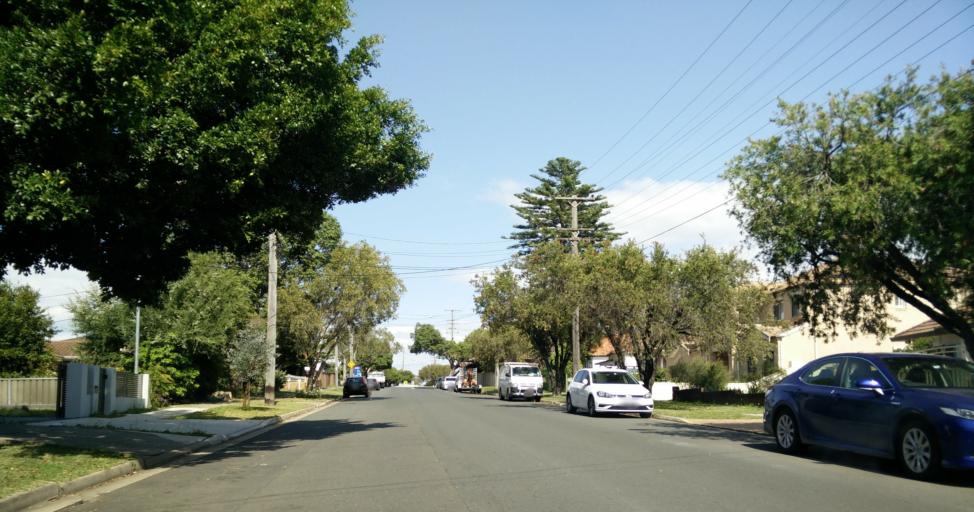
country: AU
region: New South Wales
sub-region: Bankstown
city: Padstow
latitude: -33.9503
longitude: 151.0266
